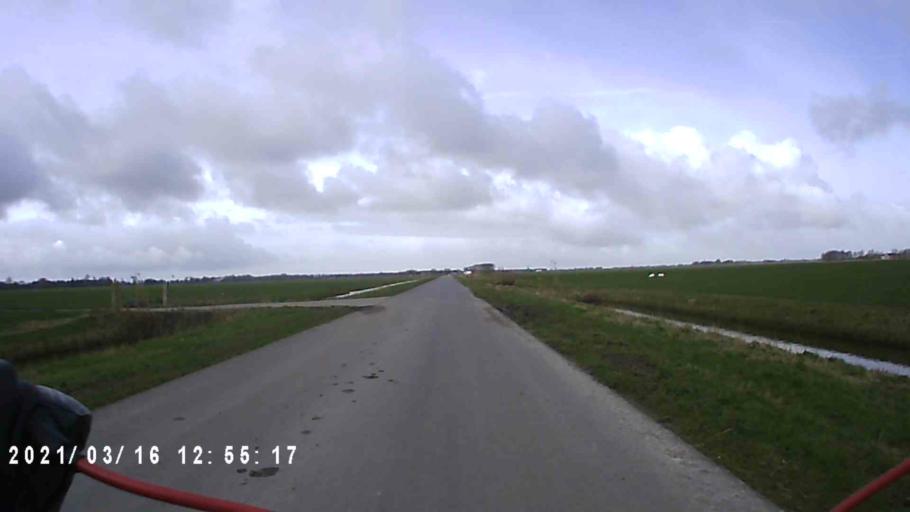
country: NL
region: Friesland
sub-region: Menameradiel
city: Berltsum
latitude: 53.2546
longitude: 5.6673
